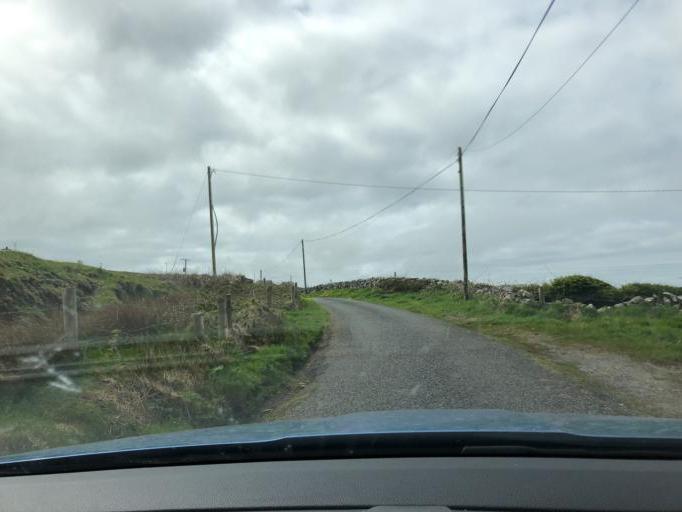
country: IE
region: Connaught
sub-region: County Galway
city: Bearna
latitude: 52.9983
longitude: -9.3989
